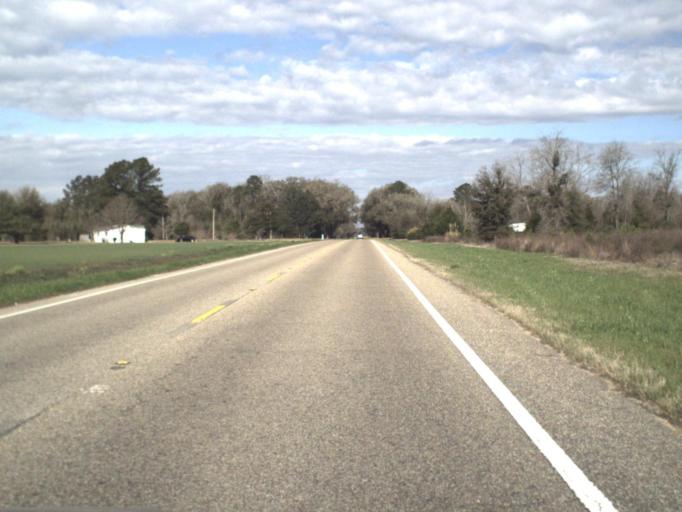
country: US
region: Florida
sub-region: Jackson County
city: Malone
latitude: 30.9809
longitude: -85.1779
